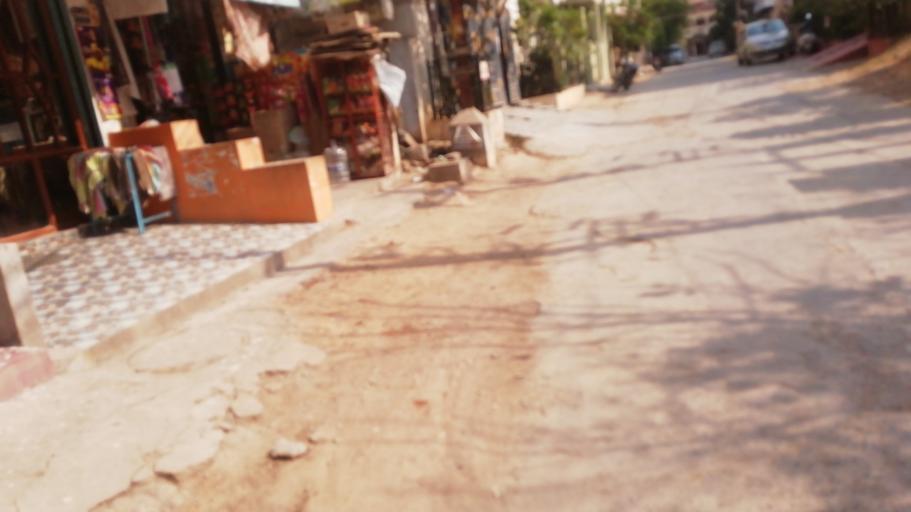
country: IN
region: Telangana
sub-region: Rangareddi
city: Gaddi Annaram
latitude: 17.3651
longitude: 78.5330
